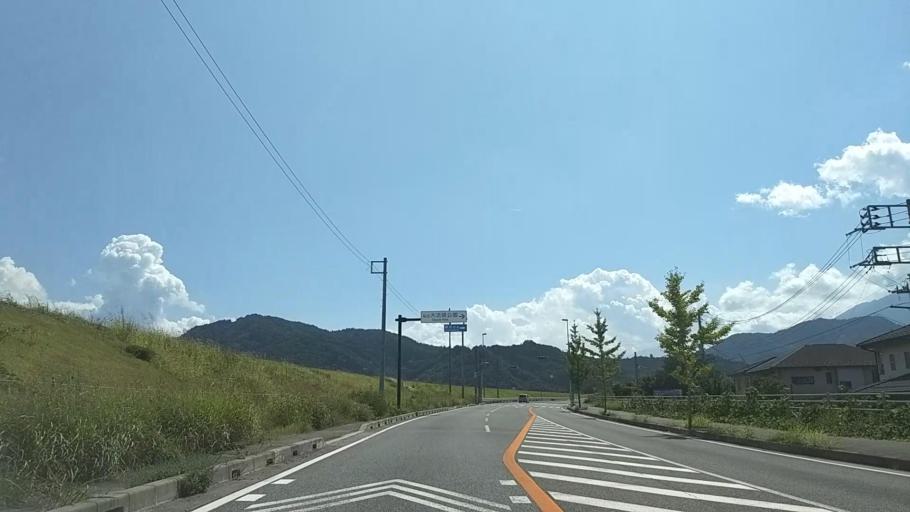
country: JP
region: Yamanashi
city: Ryuo
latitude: 35.5504
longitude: 138.4678
